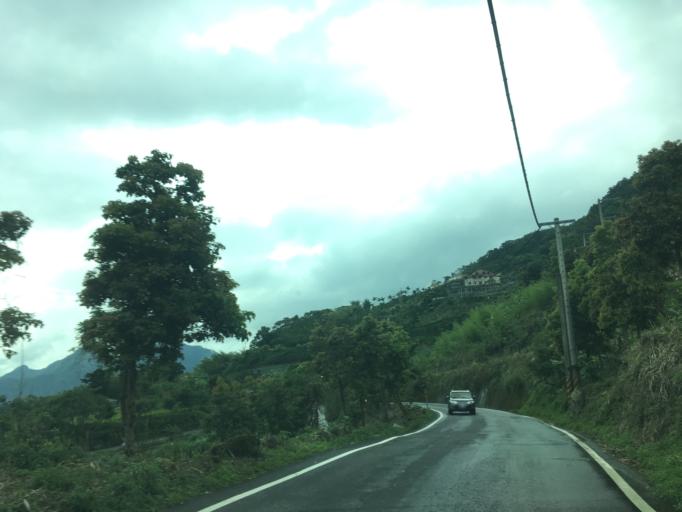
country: TW
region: Taiwan
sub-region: Chiayi
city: Jiayi Shi
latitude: 23.4452
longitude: 120.6643
